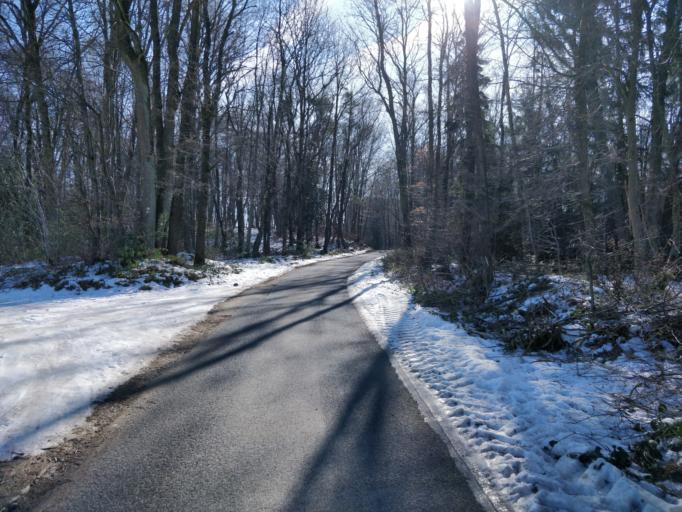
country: DE
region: North Rhine-Westphalia
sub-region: Regierungsbezirk Koln
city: Numbrecht
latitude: 50.9136
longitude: 7.5647
